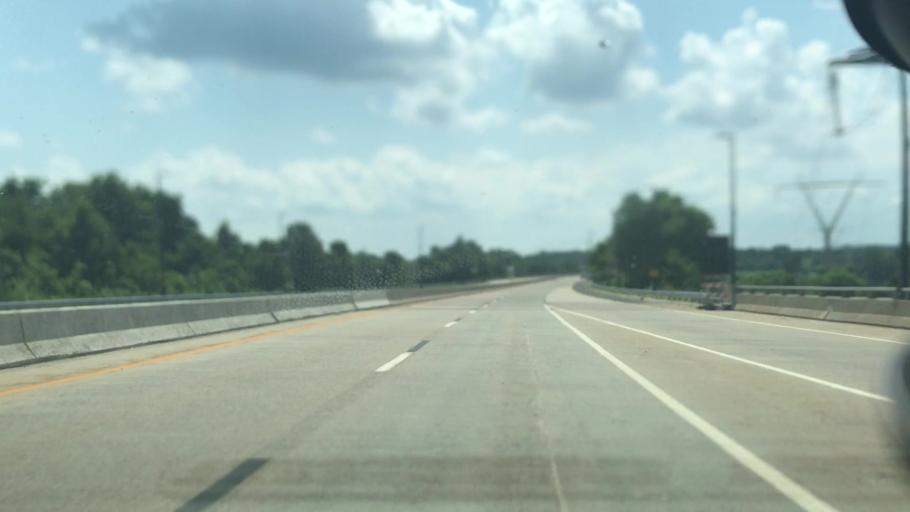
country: US
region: New Jersey
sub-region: Hunterdon County
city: Lambertville
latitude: 40.3817
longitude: -74.9499
